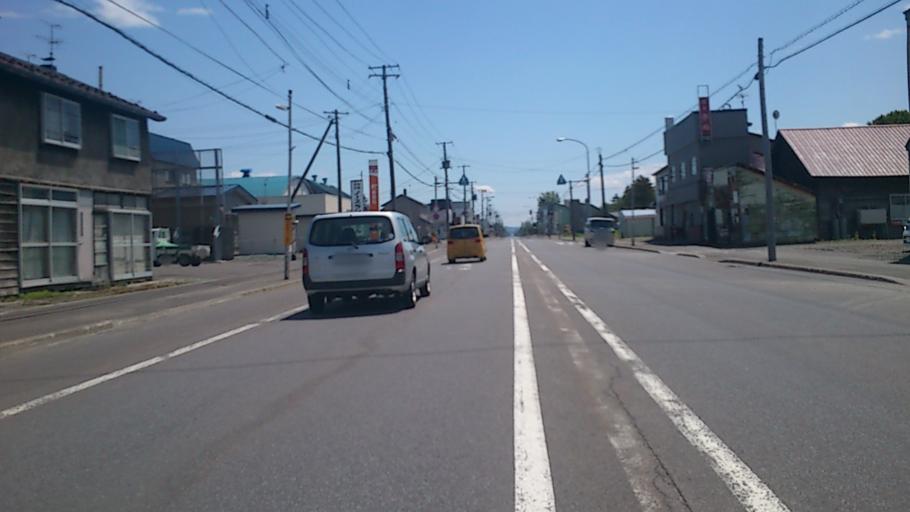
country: JP
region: Hokkaido
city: Nayoro
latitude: 44.2429
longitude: 142.3949
